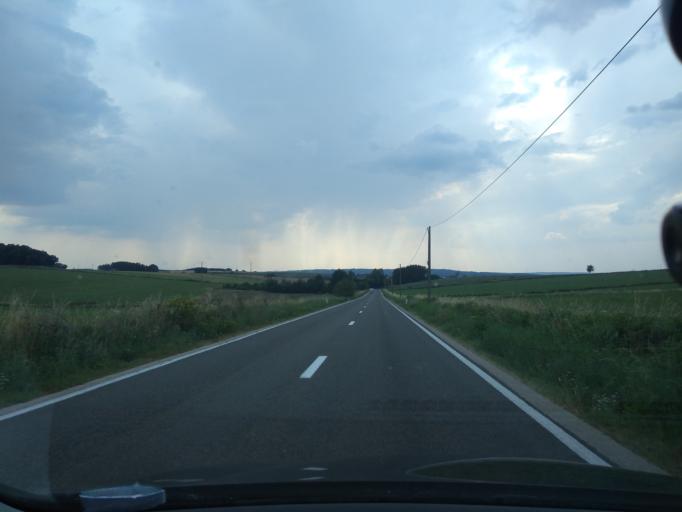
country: BE
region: Wallonia
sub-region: Province du Luxembourg
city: Bertogne
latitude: 50.0814
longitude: 5.6952
